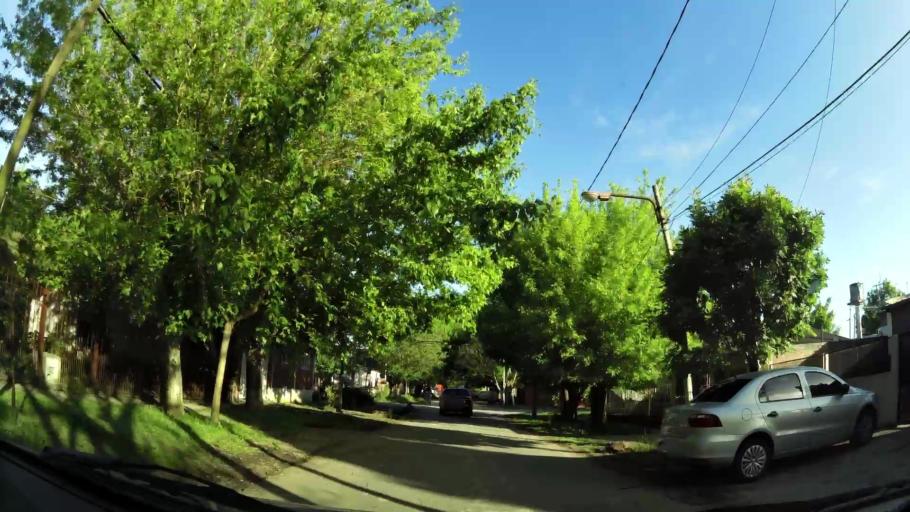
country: AR
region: Buenos Aires
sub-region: Partido de Quilmes
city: Quilmes
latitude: -34.7918
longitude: -58.2128
